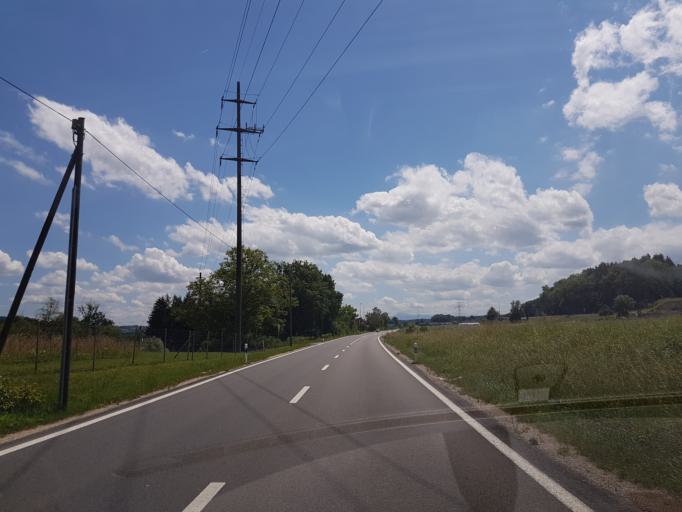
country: CH
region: Aargau
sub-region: Bezirk Baden
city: Mellingen
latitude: 47.4012
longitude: 8.2873
